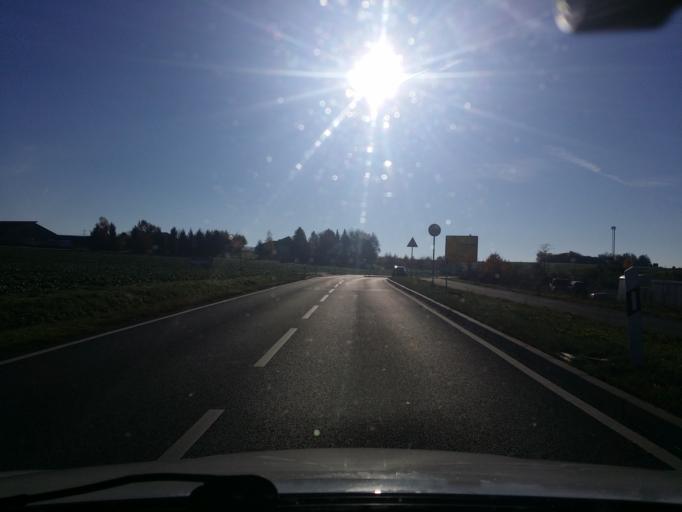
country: DE
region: Hesse
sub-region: Regierungsbezirk Darmstadt
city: Idstein
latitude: 50.2107
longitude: 8.2780
